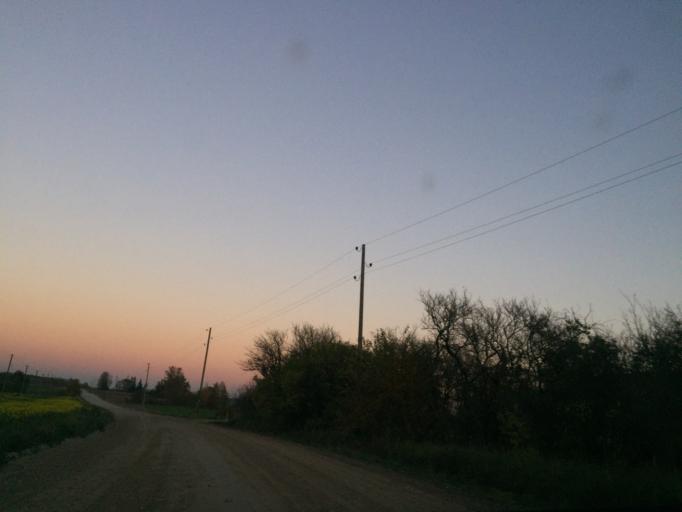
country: LT
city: Akmene
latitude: 56.3768
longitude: 22.6616
